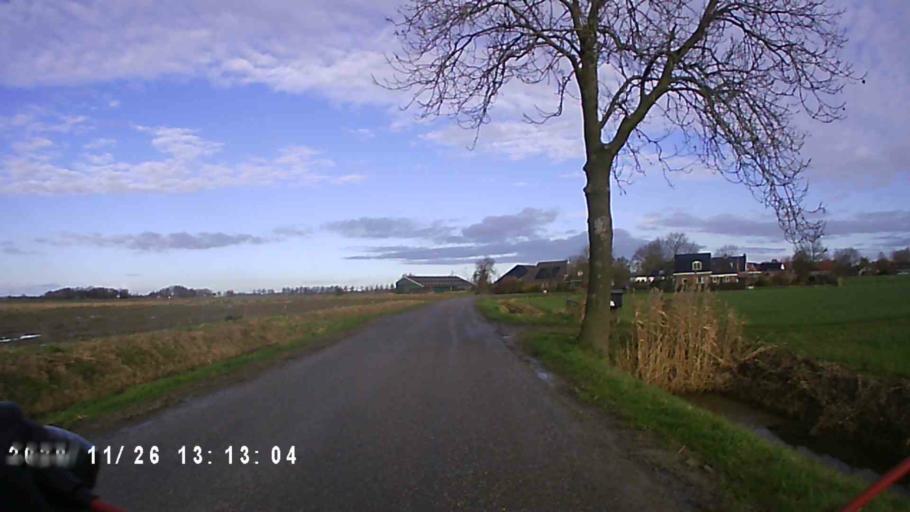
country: NL
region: Groningen
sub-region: Gemeente Appingedam
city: Appingedam
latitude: 53.3561
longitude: 6.8645
